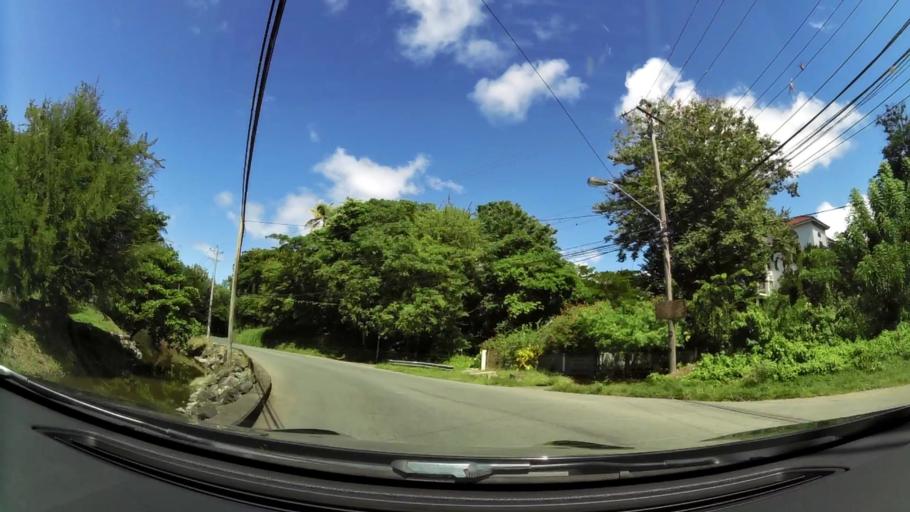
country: TT
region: Tobago
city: Scarborough
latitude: 11.2148
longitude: -60.7765
